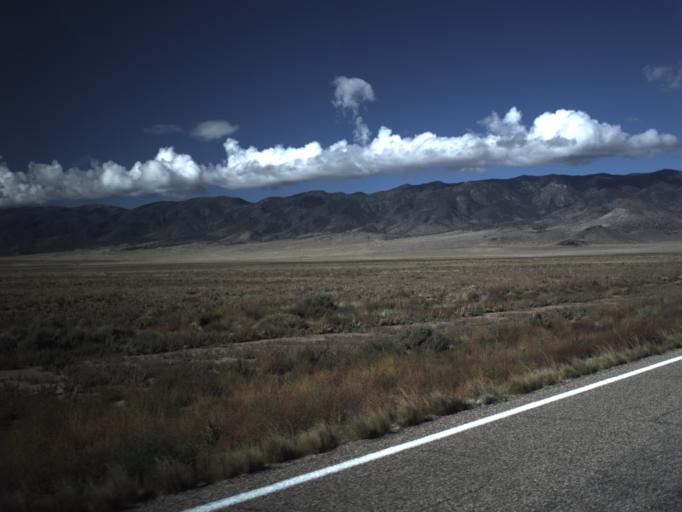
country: US
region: Utah
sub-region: Beaver County
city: Milford
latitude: 38.4694
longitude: -113.4036
